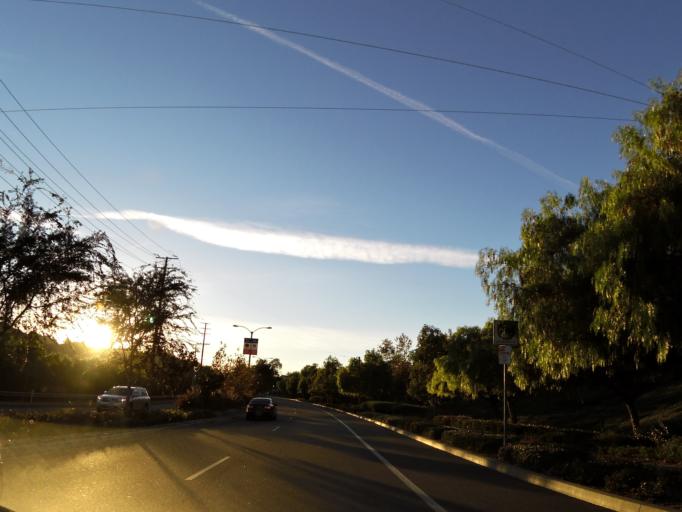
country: US
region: California
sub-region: Ventura County
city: Moorpark
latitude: 34.2637
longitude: -118.8620
